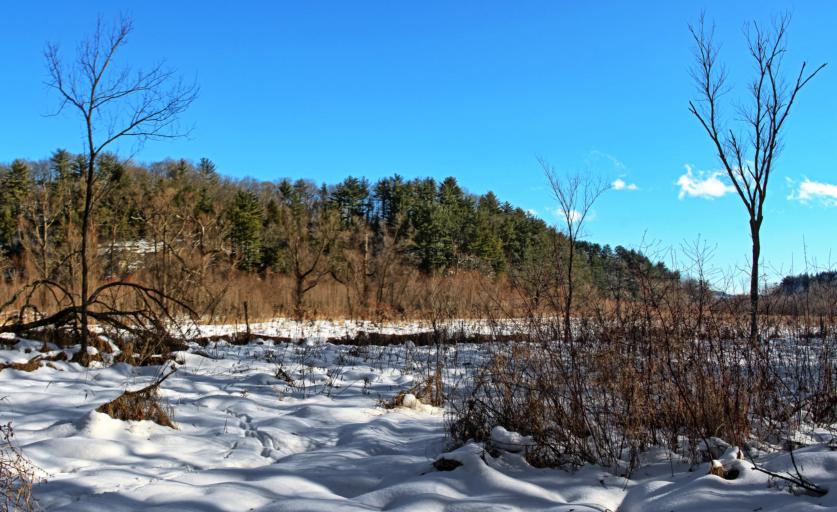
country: US
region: Wisconsin
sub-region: Sauk County
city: Reedsburg
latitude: 43.3575
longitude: -89.9829
